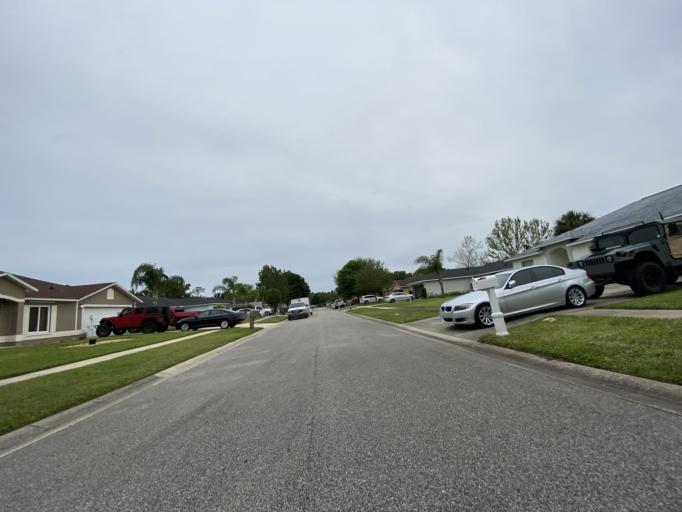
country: US
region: Florida
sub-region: Volusia County
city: South Daytona
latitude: 29.1527
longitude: -81.0007
